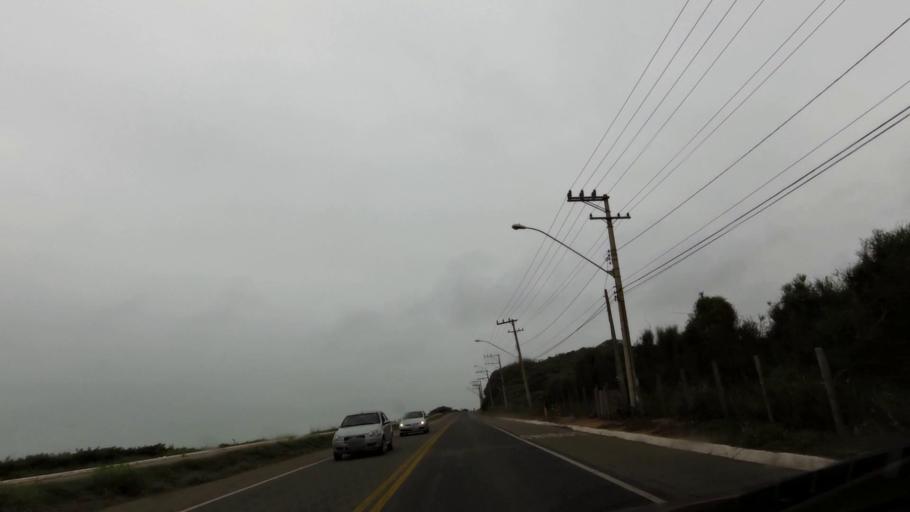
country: BR
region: Espirito Santo
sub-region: Guarapari
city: Guarapari
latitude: -20.7015
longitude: -40.5151
